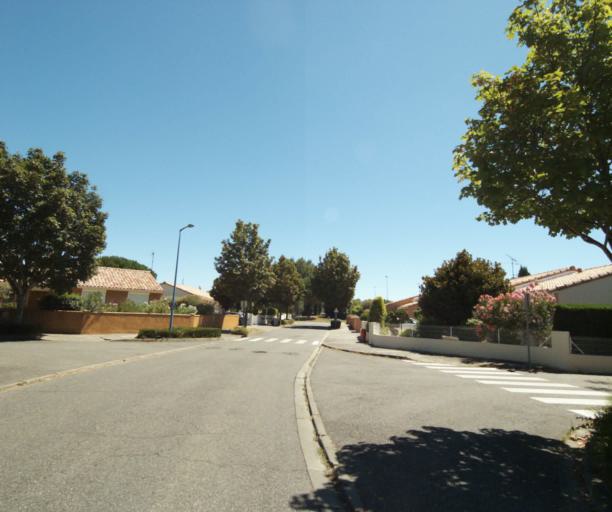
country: FR
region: Midi-Pyrenees
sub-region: Departement de la Haute-Garonne
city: Pechabou
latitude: 43.5141
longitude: 1.5102
